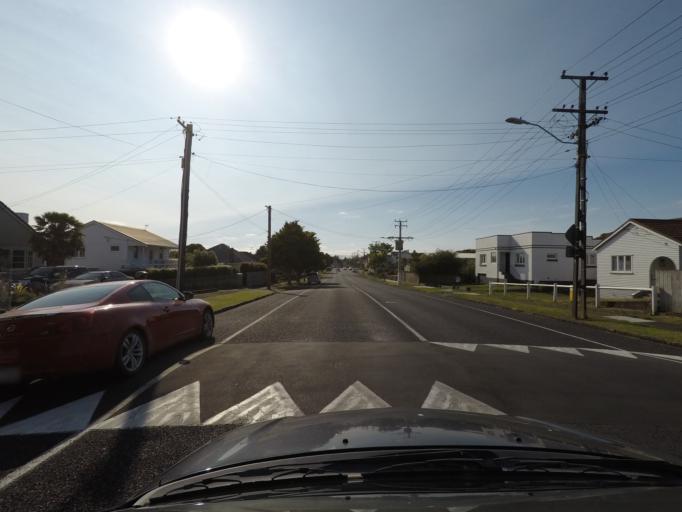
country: NZ
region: Auckland
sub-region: Auckland
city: Auckland
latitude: -36.9001
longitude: 174.7457
